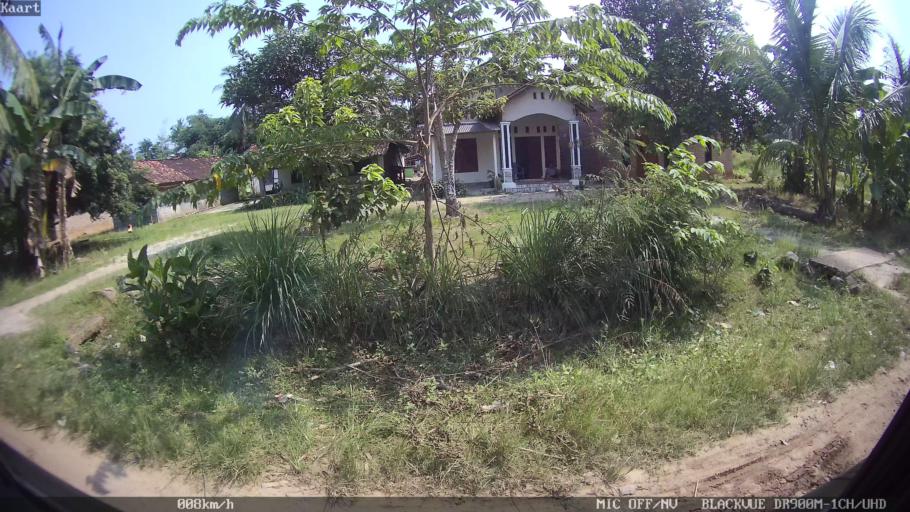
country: ID
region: Lampung
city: Natar
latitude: -5.2929
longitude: 105.2375
